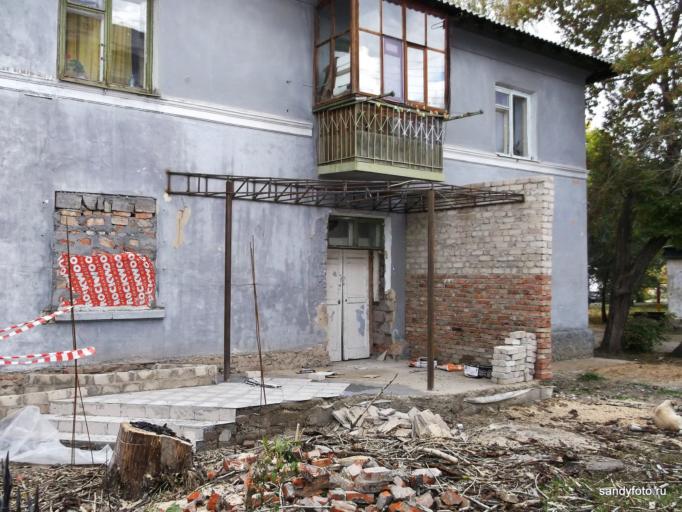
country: RU
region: Chelyabinsk
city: Troitsk
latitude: 54.0881
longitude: 61.5559
